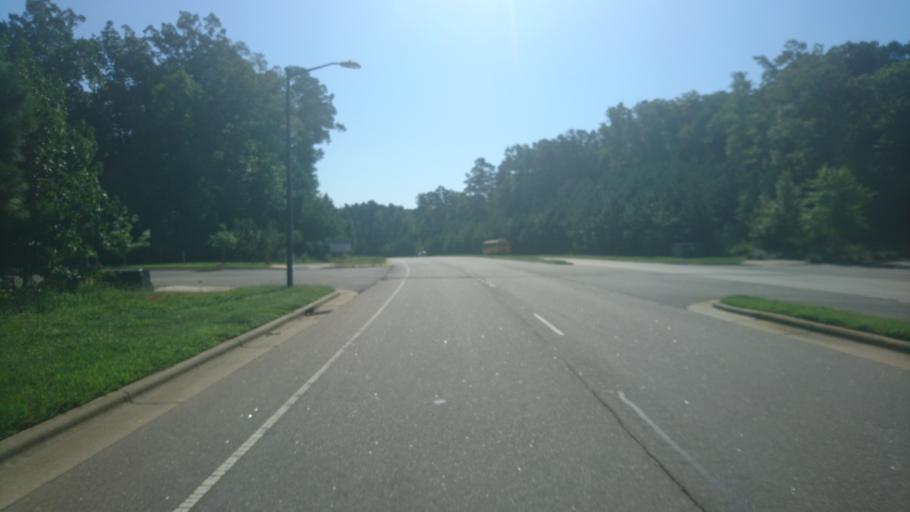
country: US
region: North Carolina
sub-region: Orange County
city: Hillsborough
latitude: 36.0378
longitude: -79.0887
